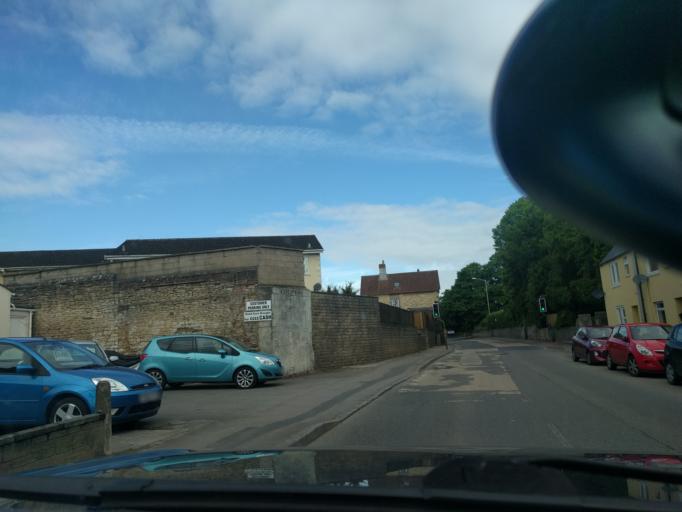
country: GB
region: England
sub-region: Wiltshire
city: Calne
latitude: 51.4395
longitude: -2.0083
